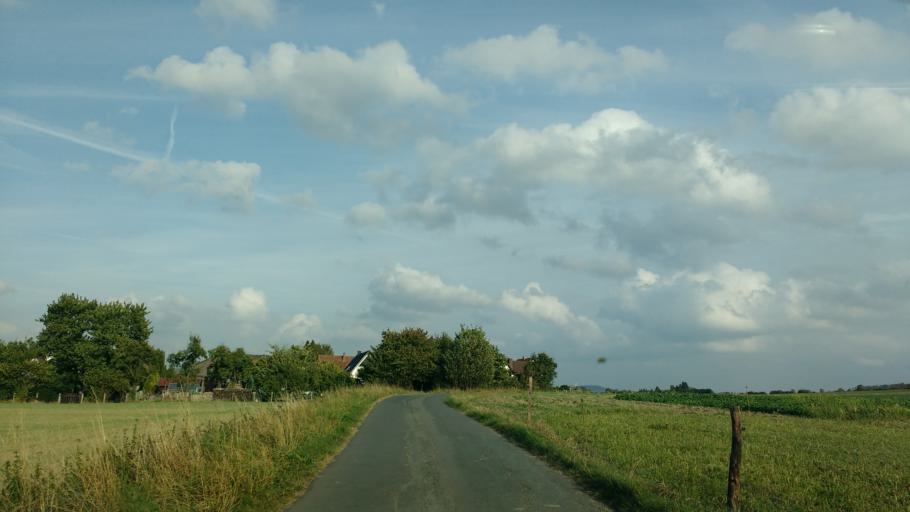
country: DE
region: North Rhine-Westphalia
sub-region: Regierungsbezirk Detmold
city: Lemgo
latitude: 52.0130
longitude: 8.8961
